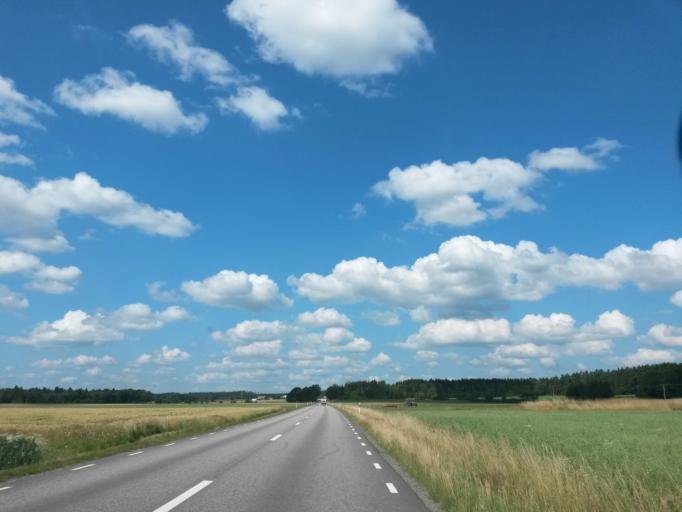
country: SE
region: Vaestra Goetaland
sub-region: Vargarda Kommun
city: Vargarda
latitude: 58.0470
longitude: 12.7858
